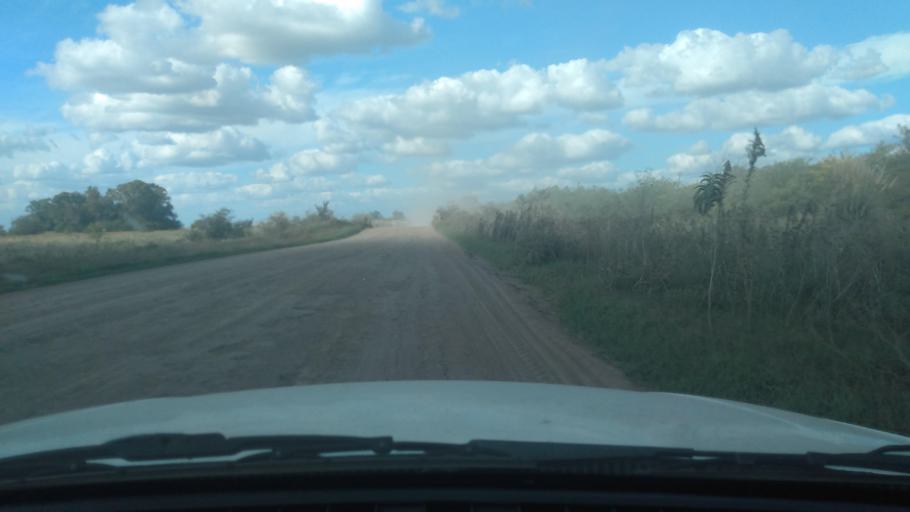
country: AR
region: Buenos Aires
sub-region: Partido de Navarro
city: Navarro
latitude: -35.0086
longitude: -59.3983
